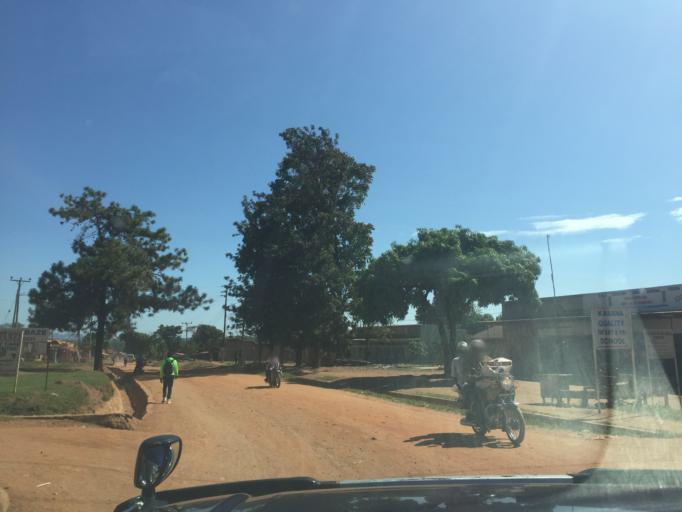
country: UG
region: Central Region
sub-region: Luwero District
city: Luwero
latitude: 0.8349
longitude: 32.5017
